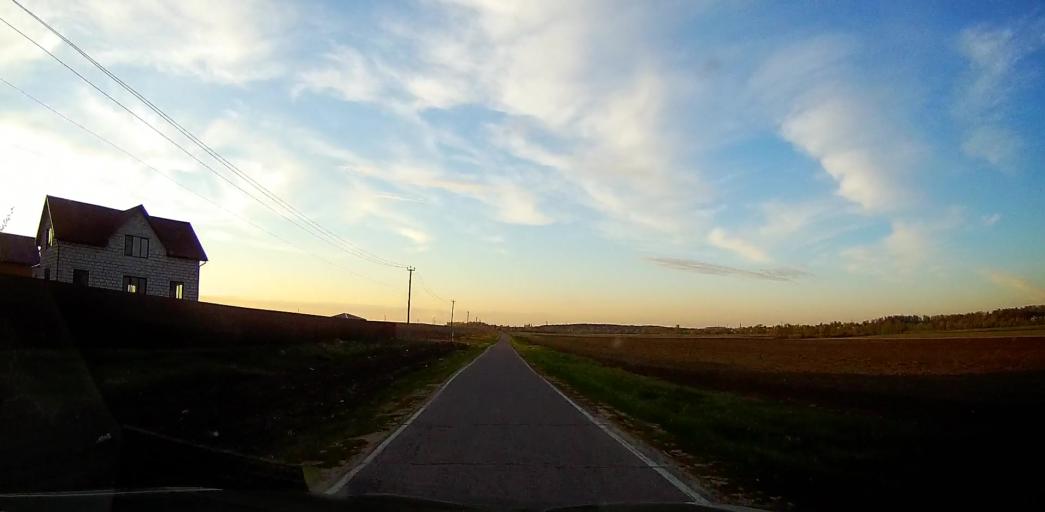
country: RU
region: Moskovskaya
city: Peski
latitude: 55.2143
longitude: 38.7393
